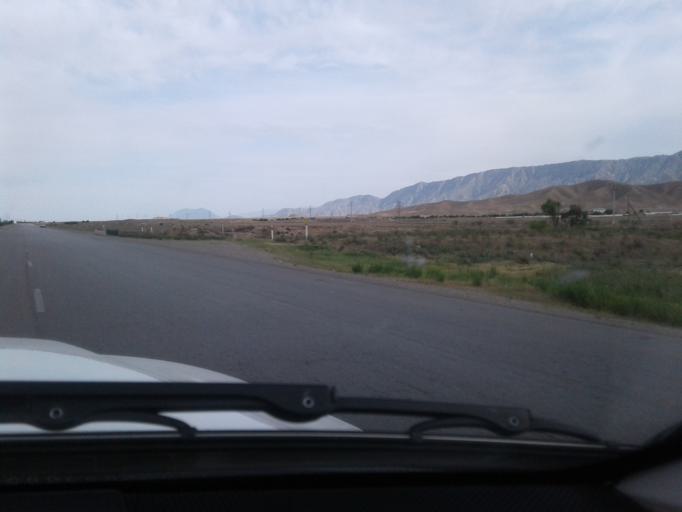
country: TM
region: Ahal
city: Baharly
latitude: 38.2405
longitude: 57.7673
